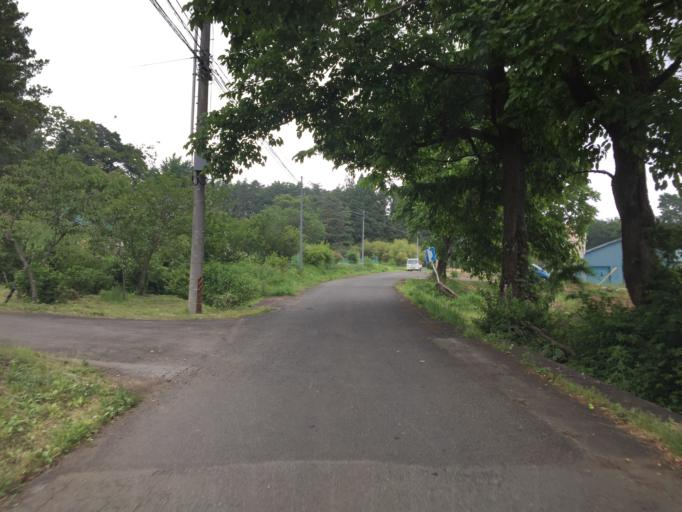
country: JP
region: Fukushima
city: Yanagawamachi-saiwaicho
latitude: 37.7653
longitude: 140.7066
